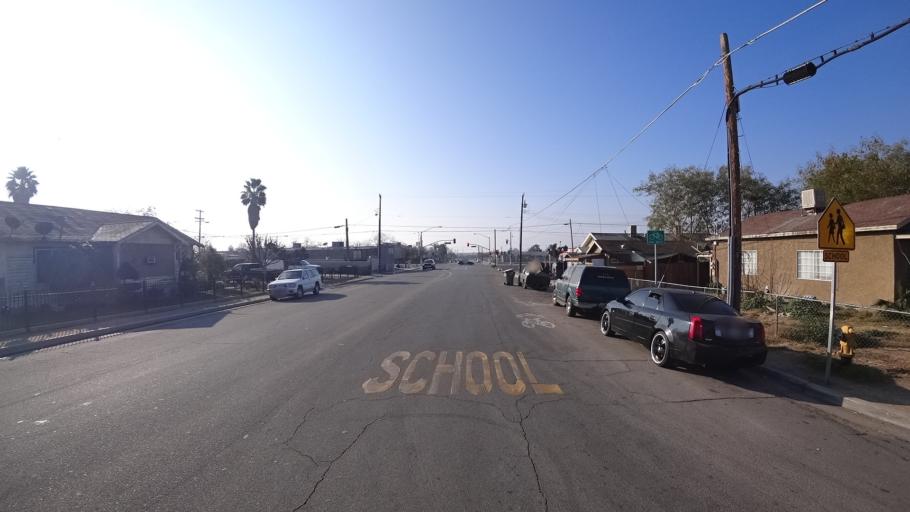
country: US
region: California
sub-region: Kern County
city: Bakersfield
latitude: 35.3793
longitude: -118.9753
